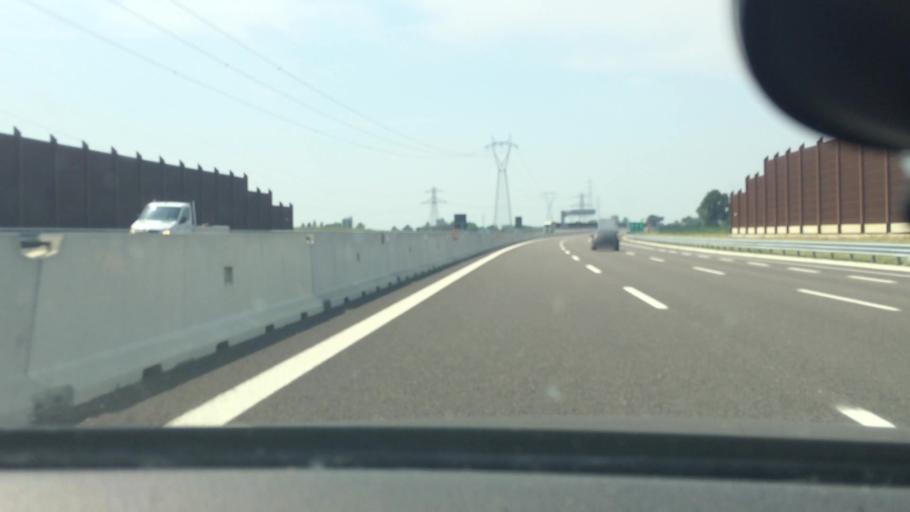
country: IT
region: Lombardy
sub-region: Provincia di Lodi
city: Zelo Buon Persico
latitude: 45.4153
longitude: 9.4168
